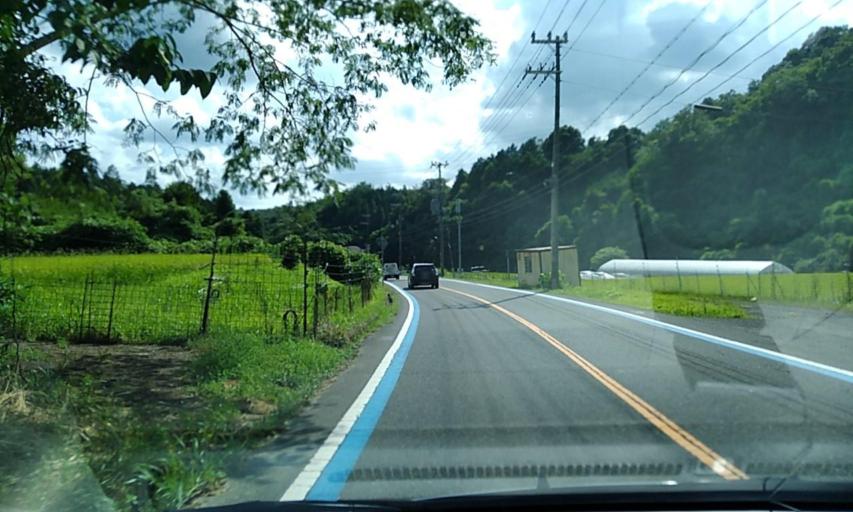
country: JP
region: Kyoto
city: Ayabe
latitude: 35.3113
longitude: 135.3015
